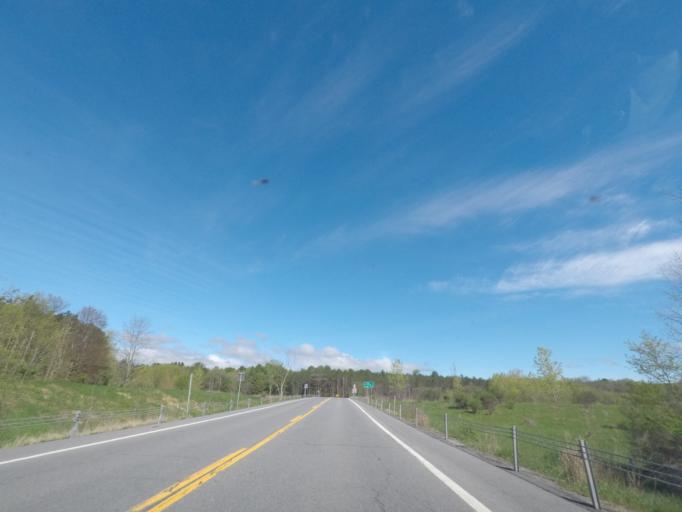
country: US
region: New York
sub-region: Albany County
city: Ravena
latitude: 42.5058
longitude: -73.9504
